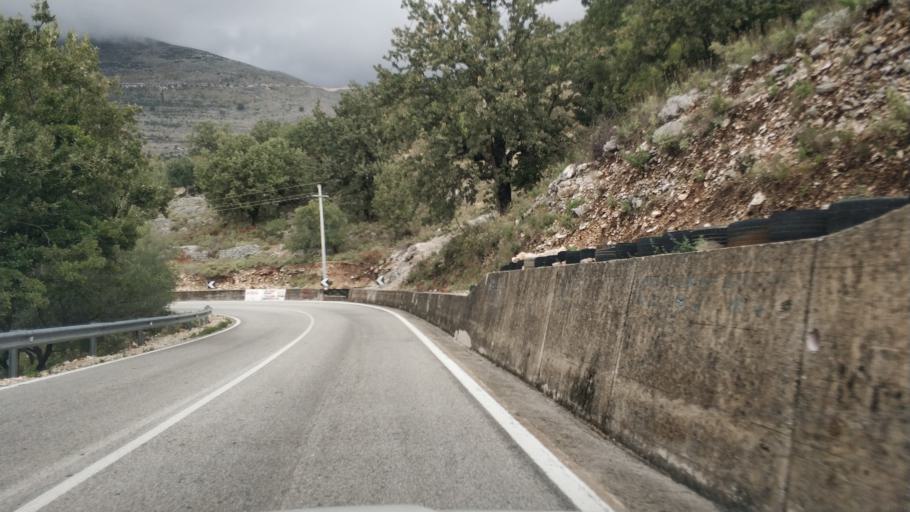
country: AL
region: Vlore
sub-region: Rrethi i Vlores
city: Vranisht
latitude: 40.1720
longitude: 19.6128
